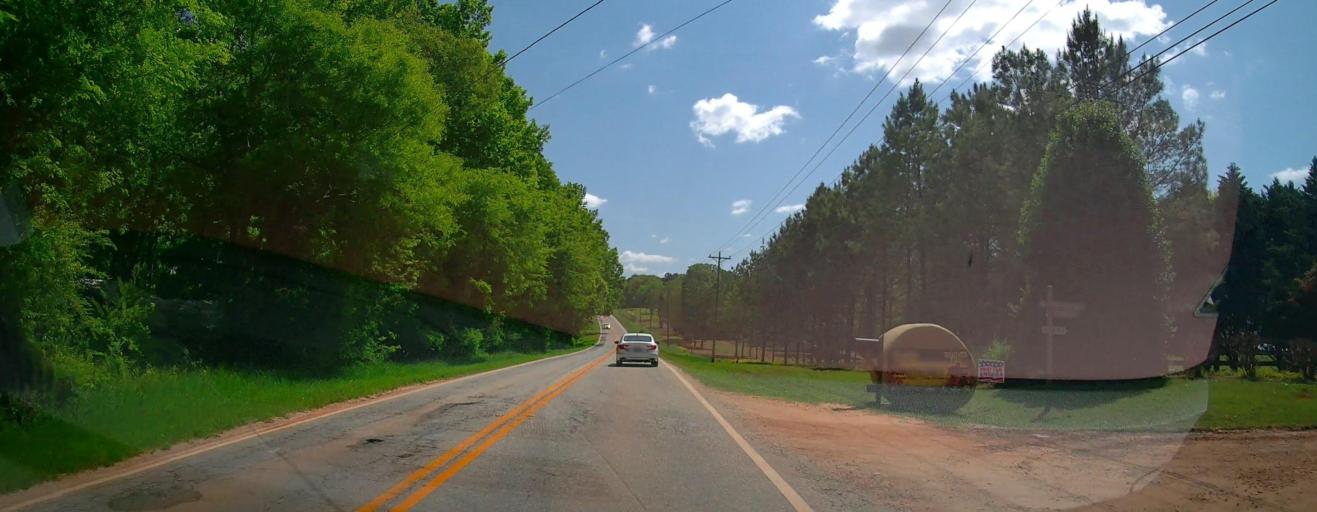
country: US
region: Georgia
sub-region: Putnam County
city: Eatonton
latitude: 33.3154
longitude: -83.2995
